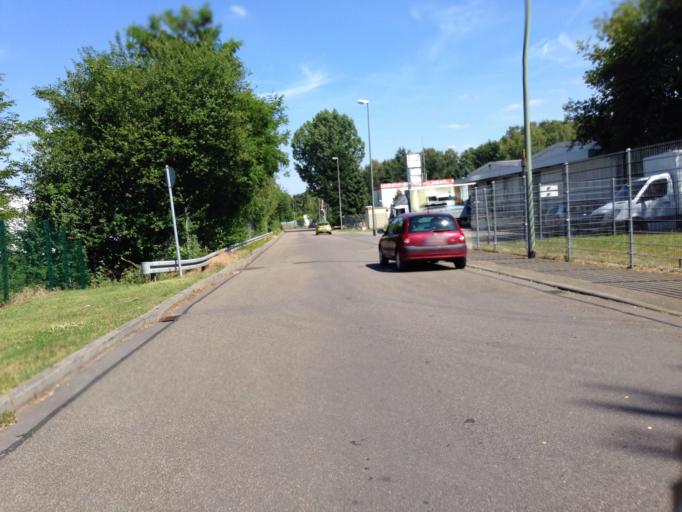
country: DE
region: Hesse
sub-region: Regierungsbezirk Darmstadt
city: Hanau am Main
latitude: 50.1117
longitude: 8.8926
